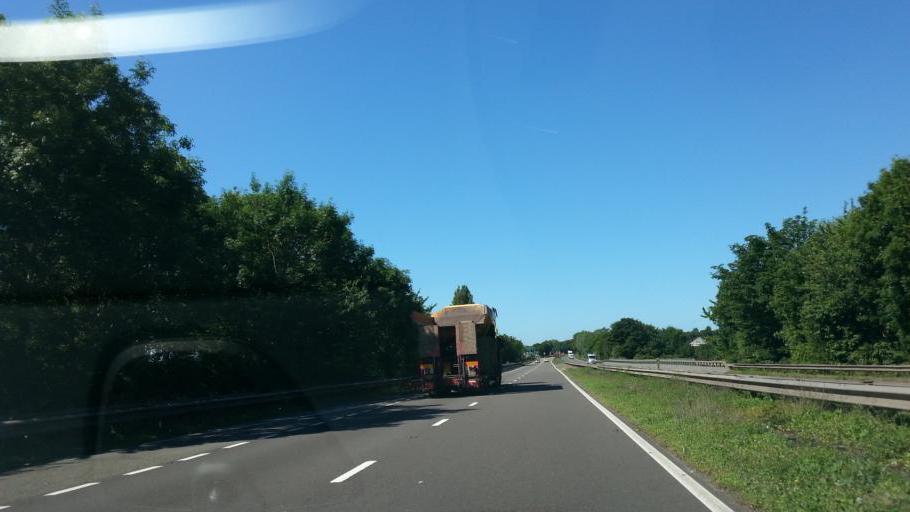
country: GB
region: England
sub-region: Herefordshire
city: Ross on Wye
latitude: 51.9200
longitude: -2.5920
